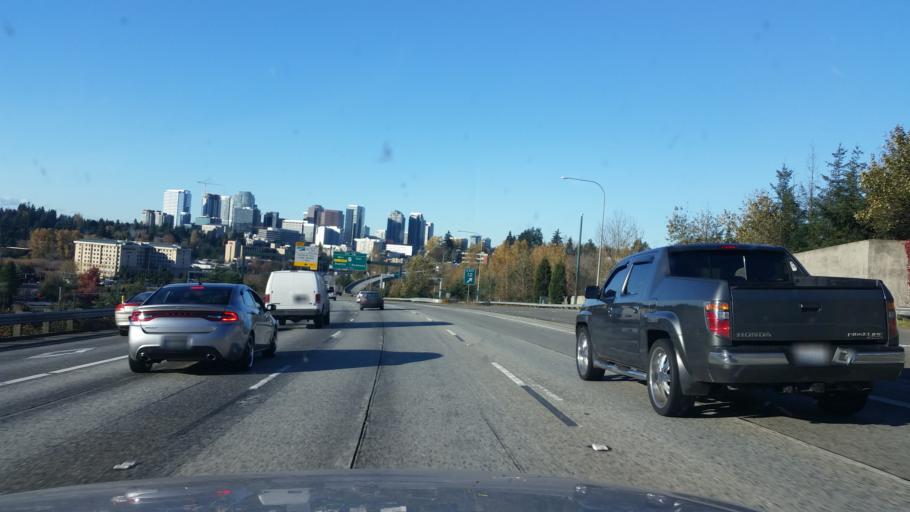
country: US
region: Washington
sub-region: King County
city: Bellevue
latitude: 47.5999
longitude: -122.1806
